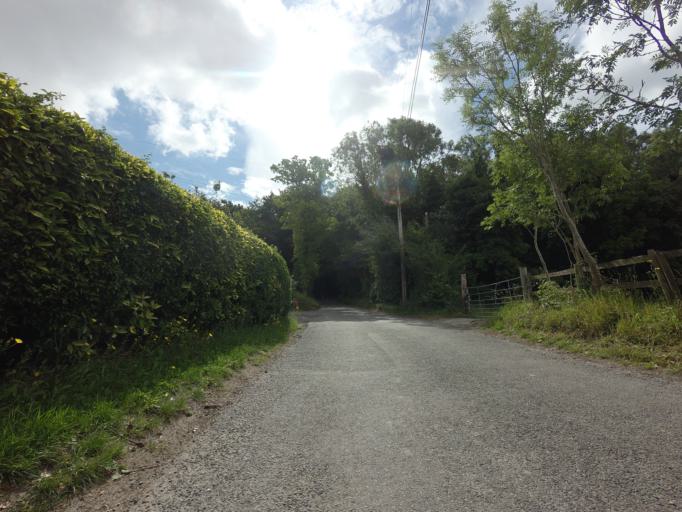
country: GB
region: England
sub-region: Kent
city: Swanley
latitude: 51.3690
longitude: 0.1446
